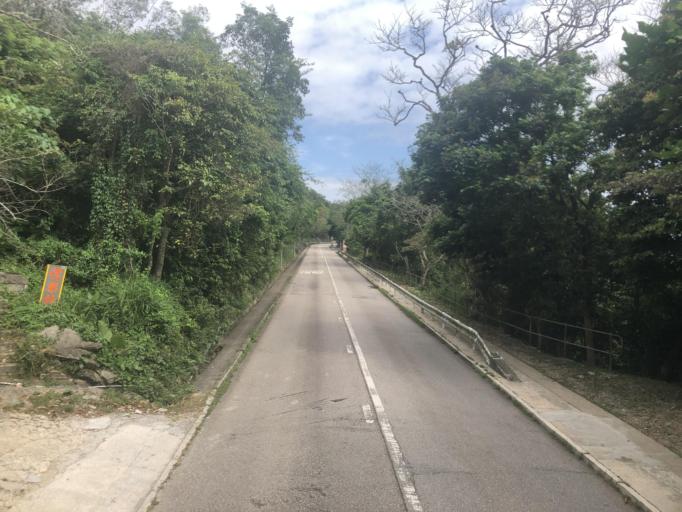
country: HK
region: Sai Kung
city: Sai Kung
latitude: 22.3895
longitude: 114.3012
